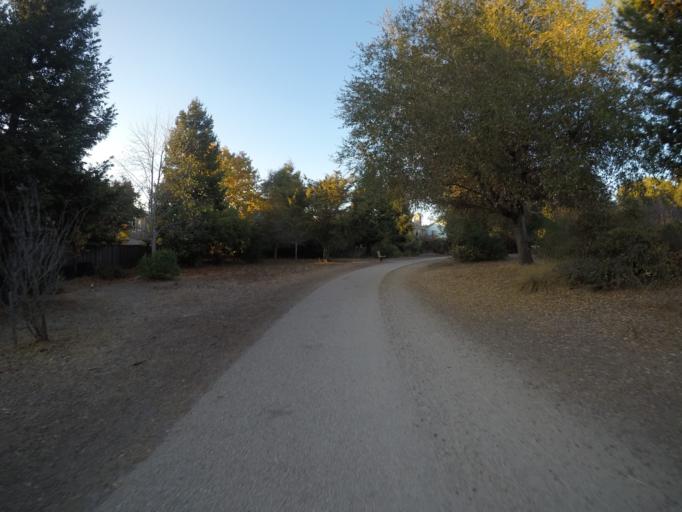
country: US
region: California
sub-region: Santa Cruz County
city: Scotts Valley
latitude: 37.0531
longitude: -122.0322
